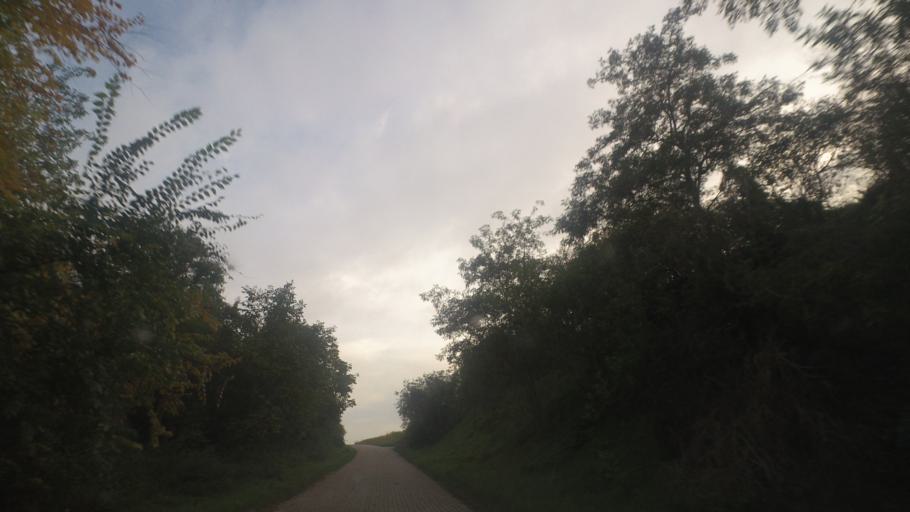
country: DE
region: Rheinland-Pfalz
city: Offstein
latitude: 49.6005
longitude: 8.2631
